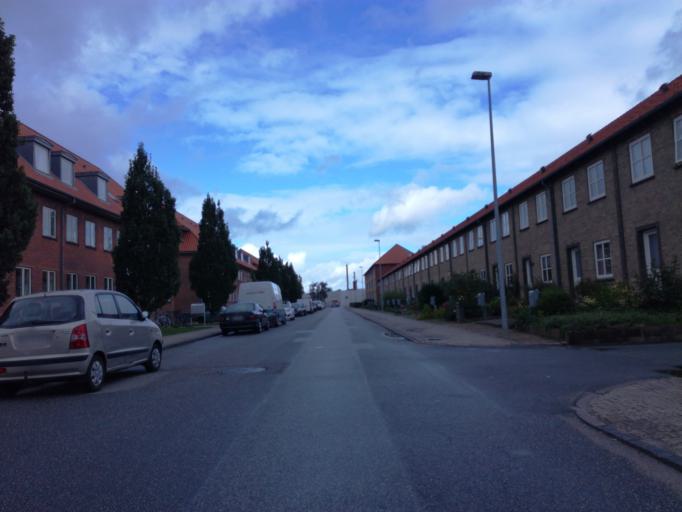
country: DK
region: South Denmark
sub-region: Fredericia Kommune
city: Fredericia
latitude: 55.5756
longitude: 9.7439
